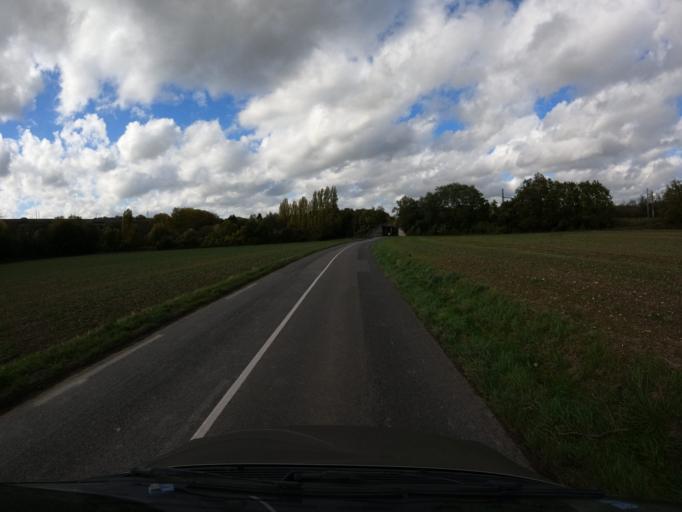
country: FR
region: Ile-de-France
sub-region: Departement de Seine-et-Marne
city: Chalifert
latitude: 48.9003
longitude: 2.7820
